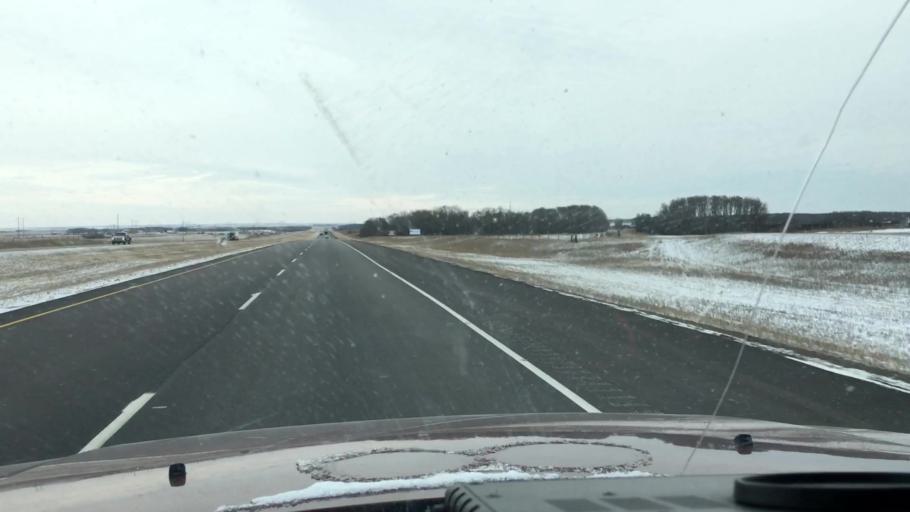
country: CA
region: Saskatchewan
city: Saskatoon
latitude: 51.9045
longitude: -106.5235
